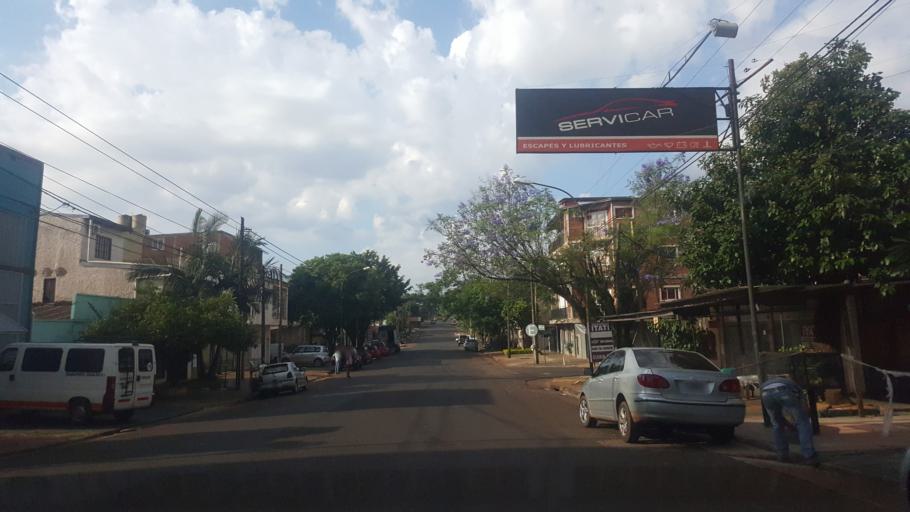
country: AR
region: Misiones
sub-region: Departamento de Capital
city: Posadas
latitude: -27.3827
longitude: -55.8959
